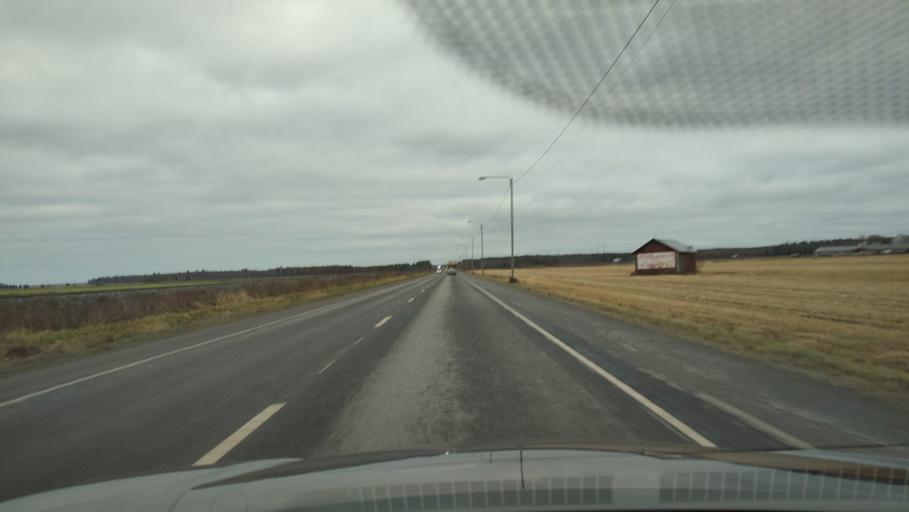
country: FI
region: Southern Ostrobothnia
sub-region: Seinaejoki
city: Ilmajoki
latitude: 62.7396
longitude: 22.6162
